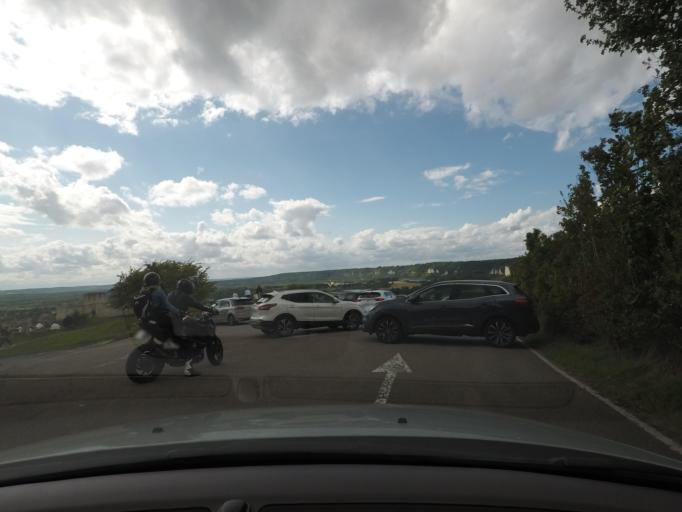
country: FR
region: Haute-Normandie
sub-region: Departement de l'Eure
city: Les Andelys
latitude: 49.2390
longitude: 1.4068
